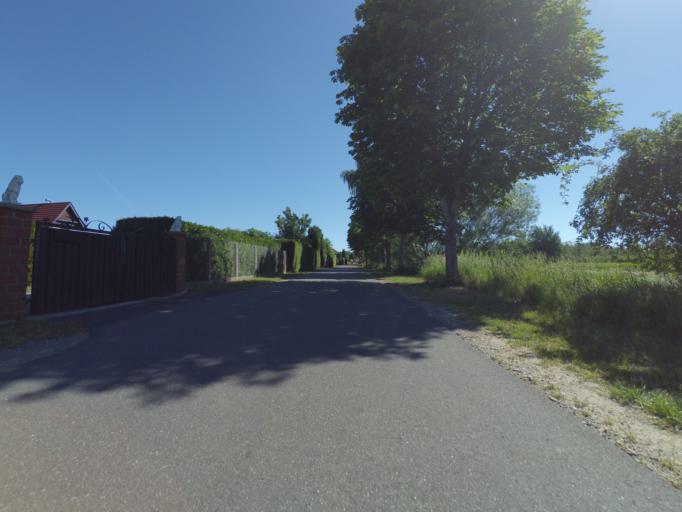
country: DE
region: Mecklenburg-Vorpommern
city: Plau am See
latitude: 53.4646
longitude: 12.2703
